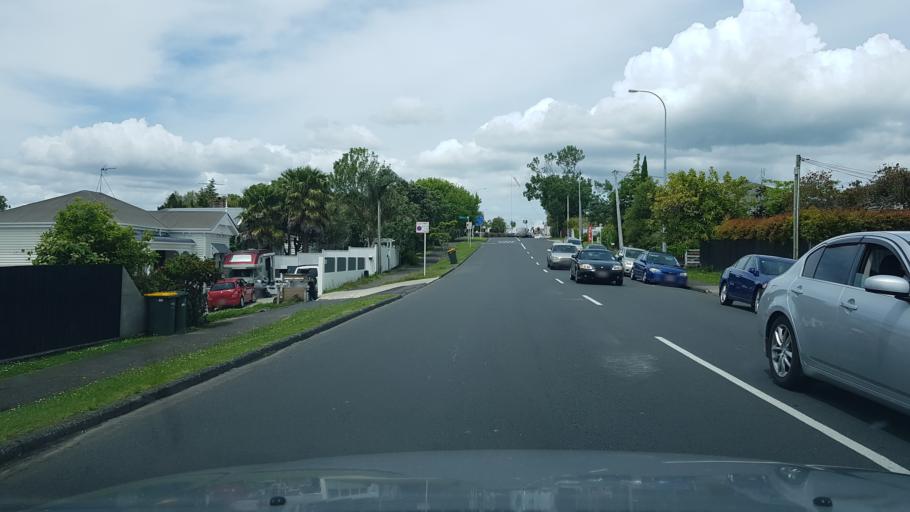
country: NZ
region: Auckland
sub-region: Auckland
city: North Shore
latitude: -36.8079
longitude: 174.7256
